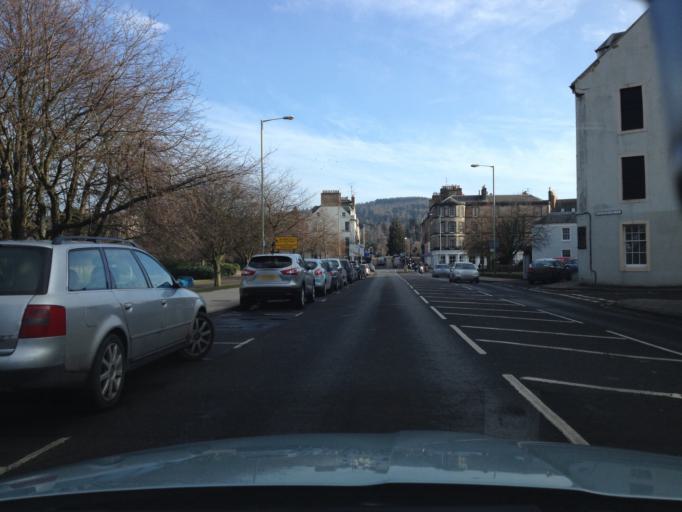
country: GB
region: Scotland
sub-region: Perth and Kinross
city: Perth
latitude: 56.3994
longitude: -3.4309
